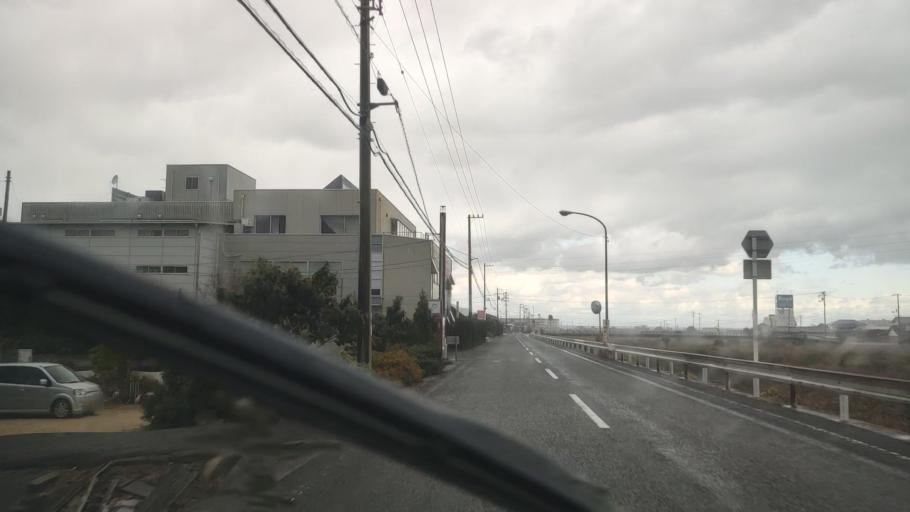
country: JP
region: Tokushima
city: Ishii
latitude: 34.2111
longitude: 134.4049
